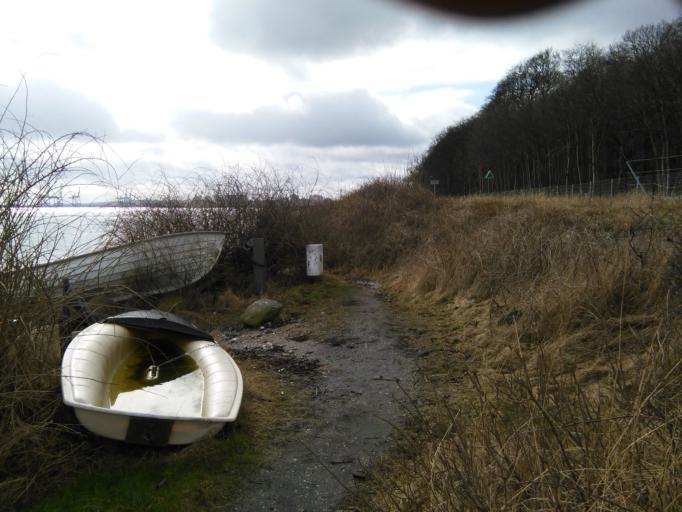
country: DK
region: Central Jutland
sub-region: Arhus Kommune
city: Arhus
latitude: 56.1807
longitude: 10.2349
